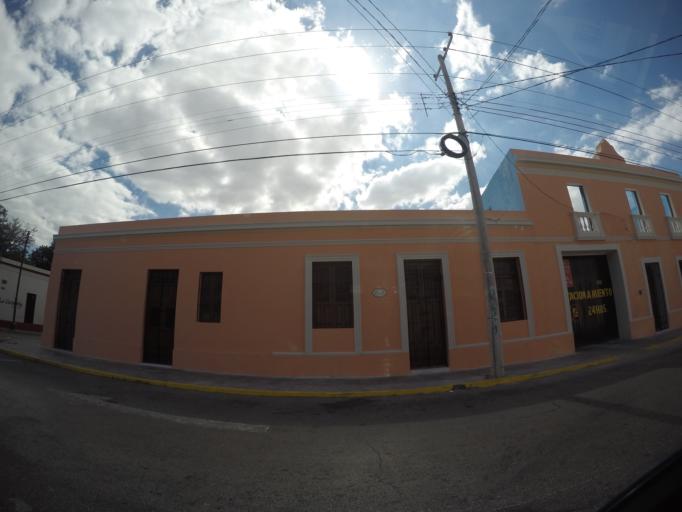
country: MX
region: Yucatan
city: Merida
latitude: 20.9747
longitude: -89.6164
